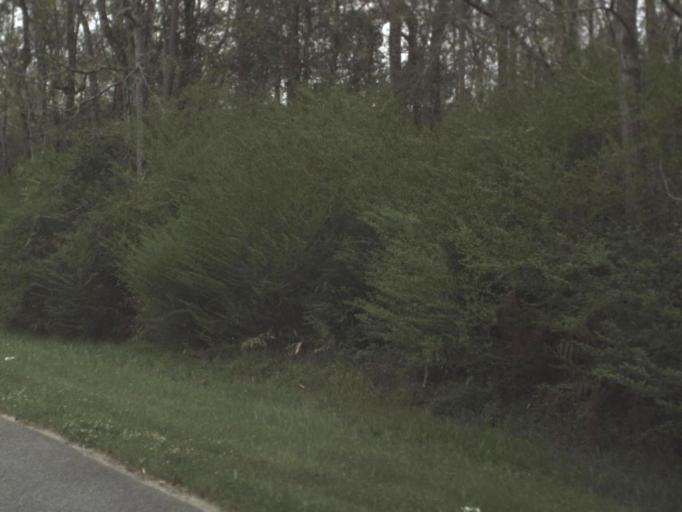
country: US
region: Florida
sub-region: Jackson County
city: Graceville
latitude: 30.9691
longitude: -85.6466
